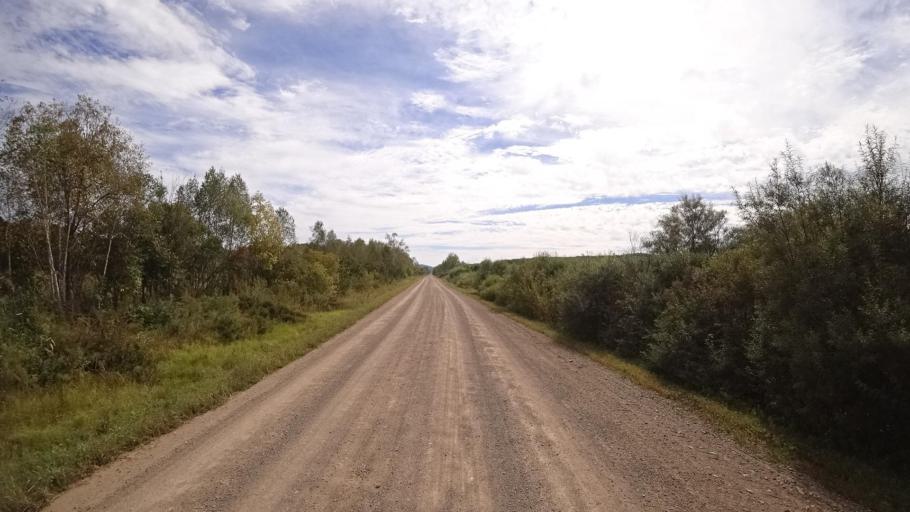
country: RU
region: Primorskiy
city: Yakovlevka
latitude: 44.6178
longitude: 133.5968
